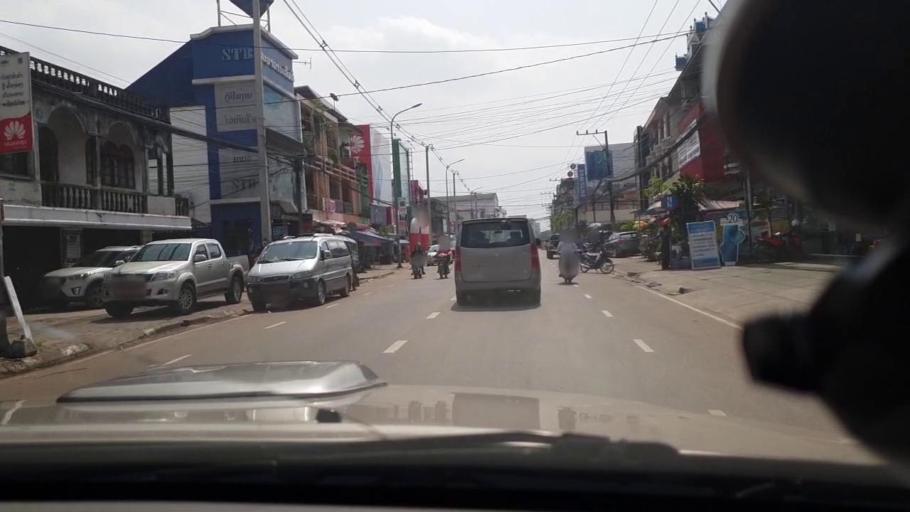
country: LA
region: Vientiane
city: Vientiane
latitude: 17.9622
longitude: 102.6219
